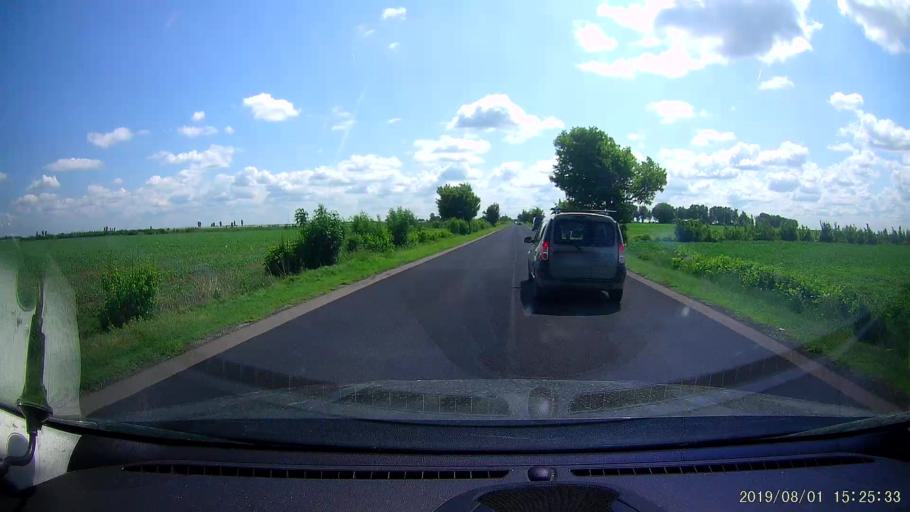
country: RO
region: Braila
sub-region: Comuna Viziru
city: Lanurile
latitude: 45.0205
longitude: 27.7336
